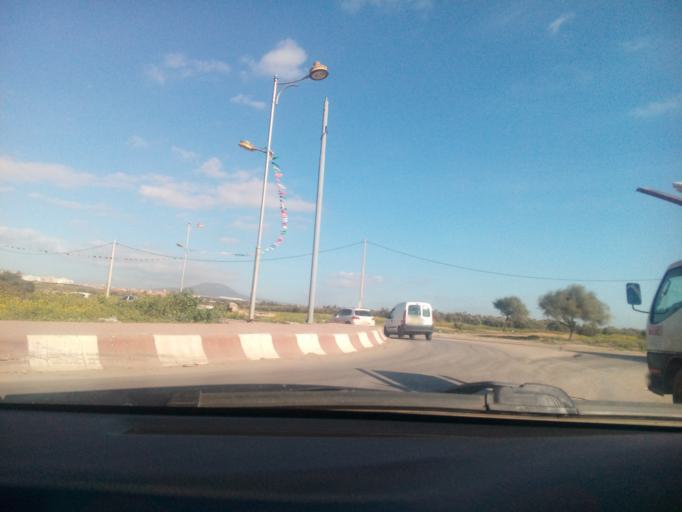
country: DZ
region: Oran
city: Sidi ech Chahmi
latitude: 35.6689
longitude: -0.5661
